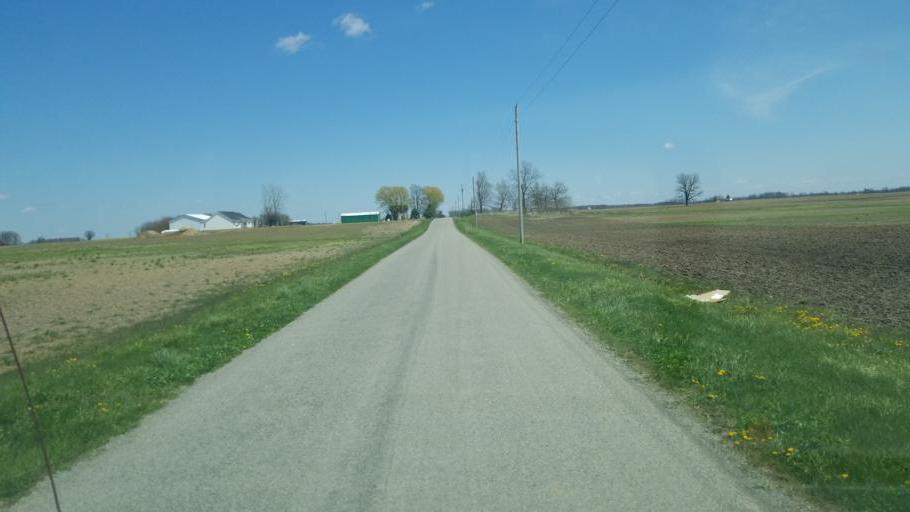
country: US
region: Ohio
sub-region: Union County
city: Richwood
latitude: 40.4917
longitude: -83.2796
